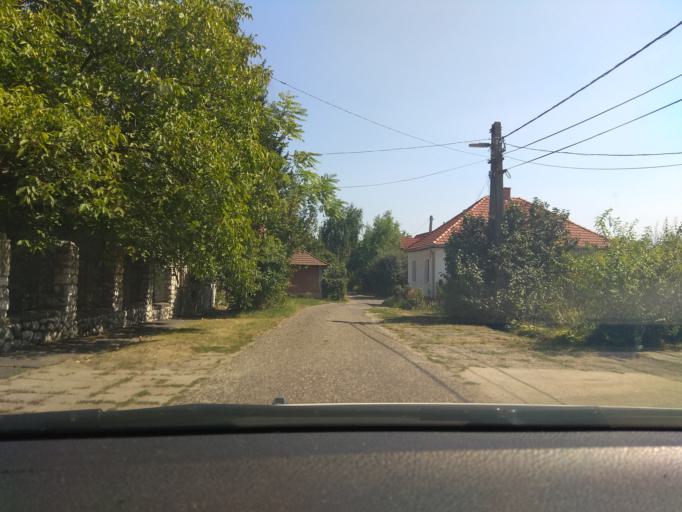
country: HU
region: Borsod-Abauj-Zemplen
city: Miskolc
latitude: 48.0744
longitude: 20.7836
